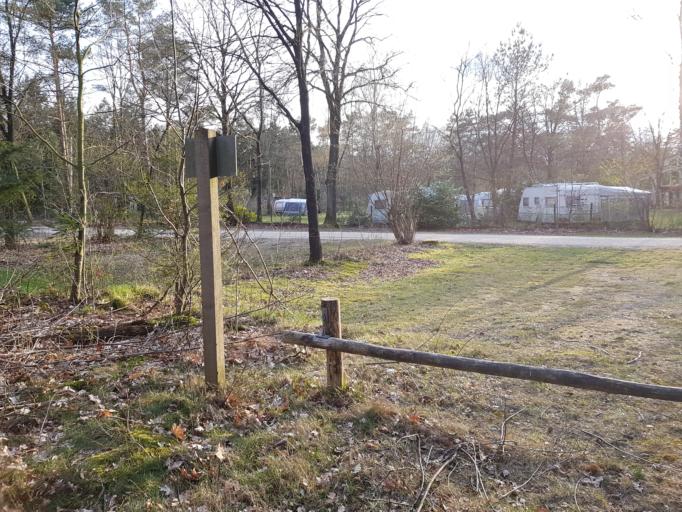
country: NL
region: Gelderland
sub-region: Gemeente Epe
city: Emst
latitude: 52.3152
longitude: 5.9313
